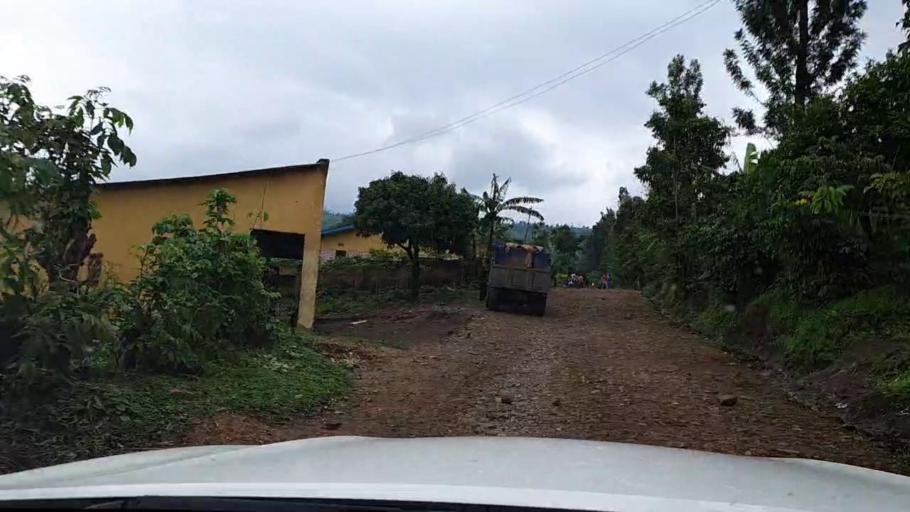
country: RW
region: Western Province
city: Cyangugu
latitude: -2.5469
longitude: 29.0379
